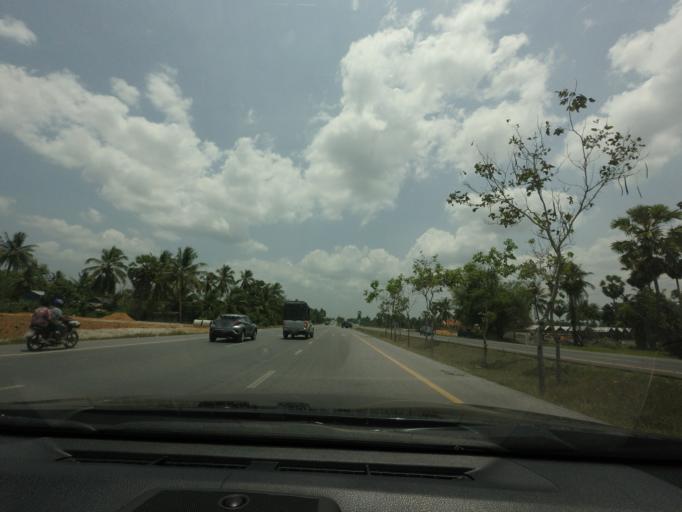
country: TH
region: Pattani
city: Pattani
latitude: 6.8497
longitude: 101.2238
